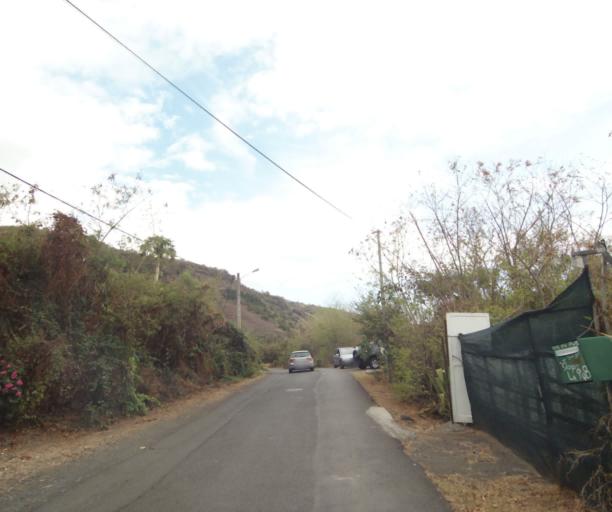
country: RE
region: Reunion
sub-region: Reunion
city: Saint-Paul
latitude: -21.0027
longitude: 55.3001
